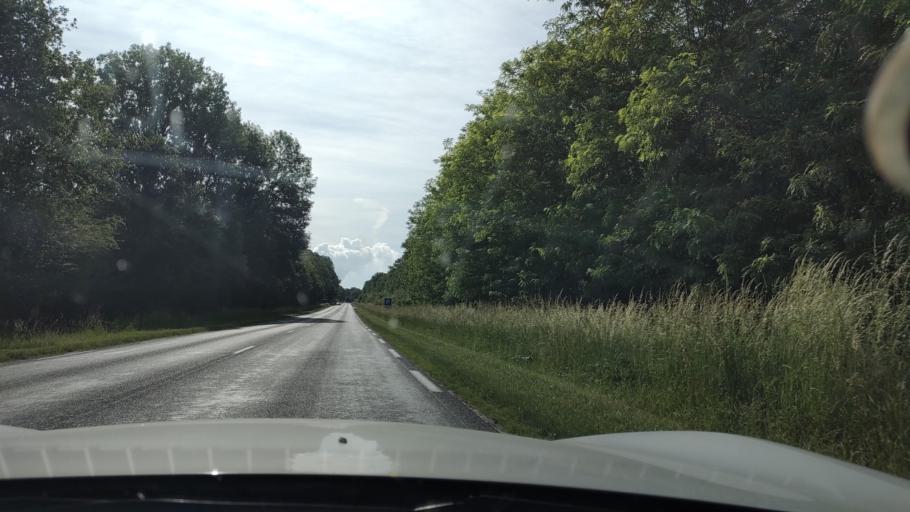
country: FR
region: Ile-de-France
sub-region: Departement de Seine-et-Marne
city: Sourdun
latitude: 48.5307
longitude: 3.3901
